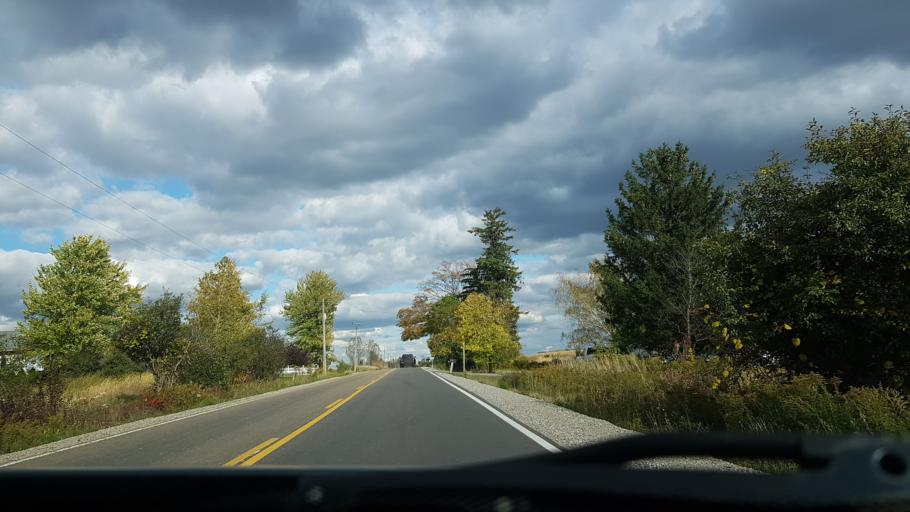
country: CA
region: Ontario
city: London
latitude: 43.0225
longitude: -81.3425
